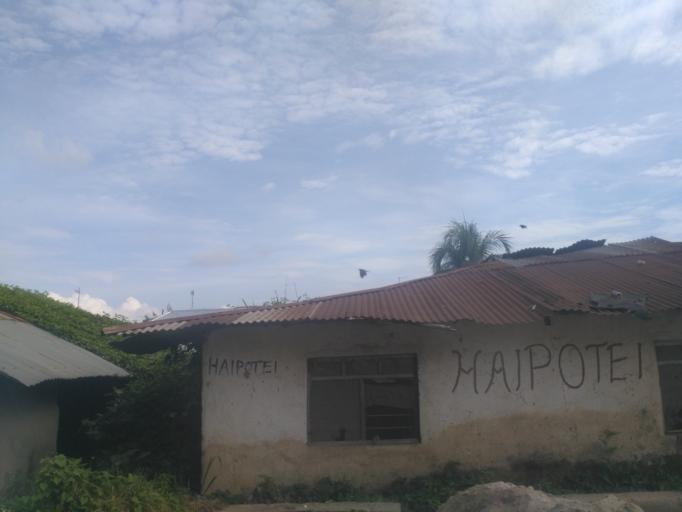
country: TZ
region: Zanzibar Urban/West
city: Zanzibar
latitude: -6.1525
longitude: 39.2102
